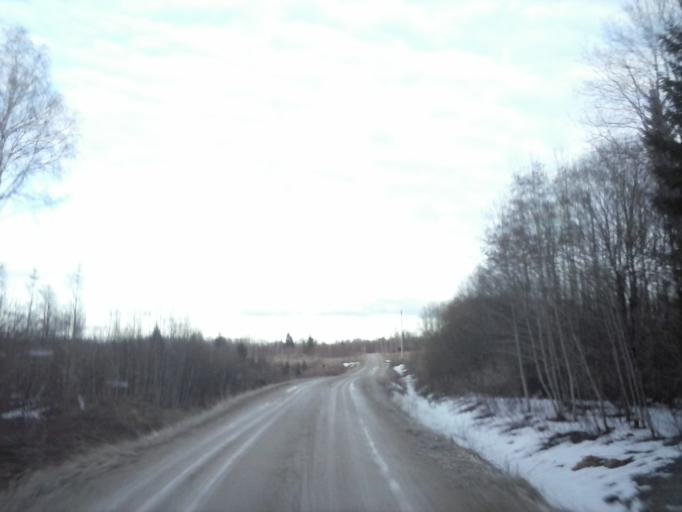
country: EE
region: Ida-Virumaa
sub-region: Johvi vald
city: Johvi
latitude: 59.1724
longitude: 27.3374
